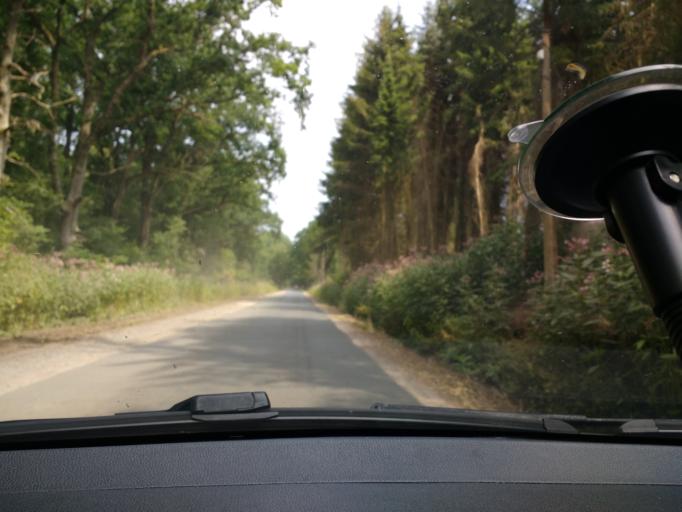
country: DE
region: Lower Saxony
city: Wagenhoff
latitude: 52.5178
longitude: 10.5522
